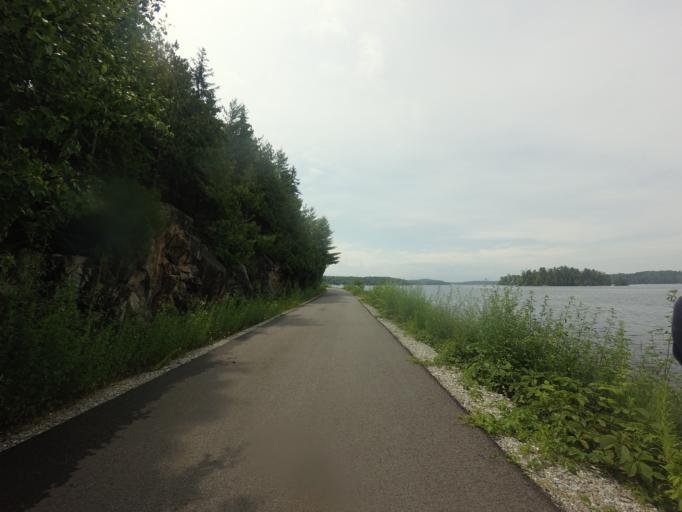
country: CA
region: Quebec
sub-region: Outaouais
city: Maniwaki
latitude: 46.2156
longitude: -76.0441
